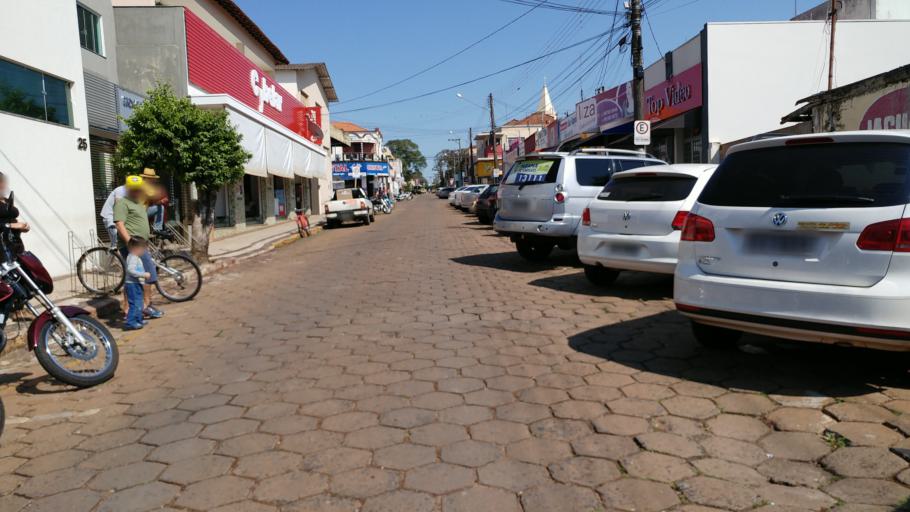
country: BR
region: Sao Paulo
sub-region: Paraguacu Paulista
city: Paraguacu Paulista
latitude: -22.4153
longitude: -50.5739
